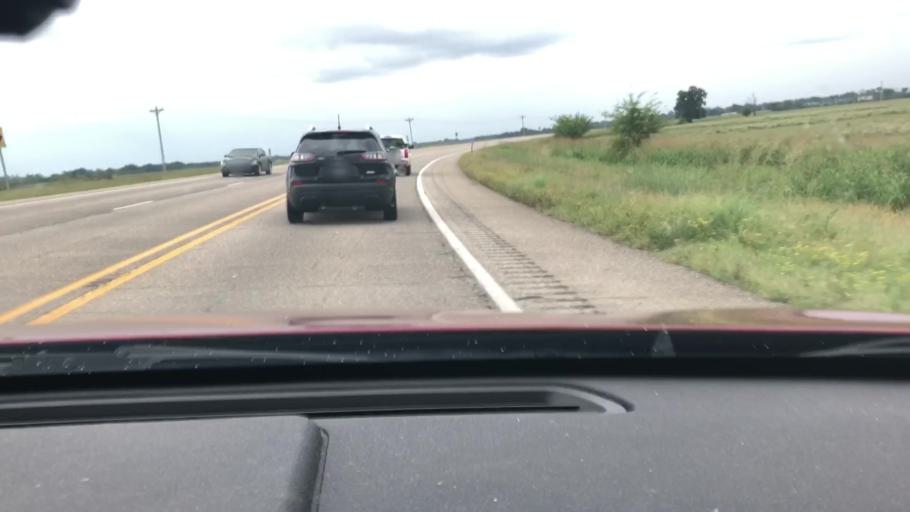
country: US
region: Arkansas
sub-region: Lafayette County
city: Lewisville
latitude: 33.3912
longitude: -93.7368
